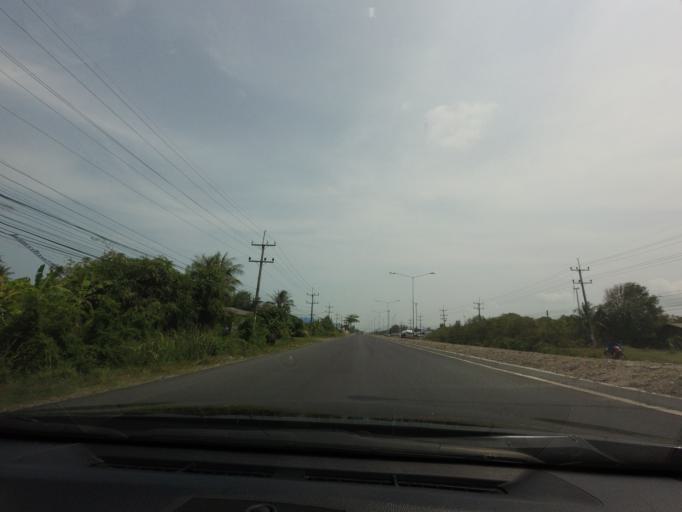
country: TH
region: Songkhla
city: Ranot
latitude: 7.8543
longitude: 100.3508
